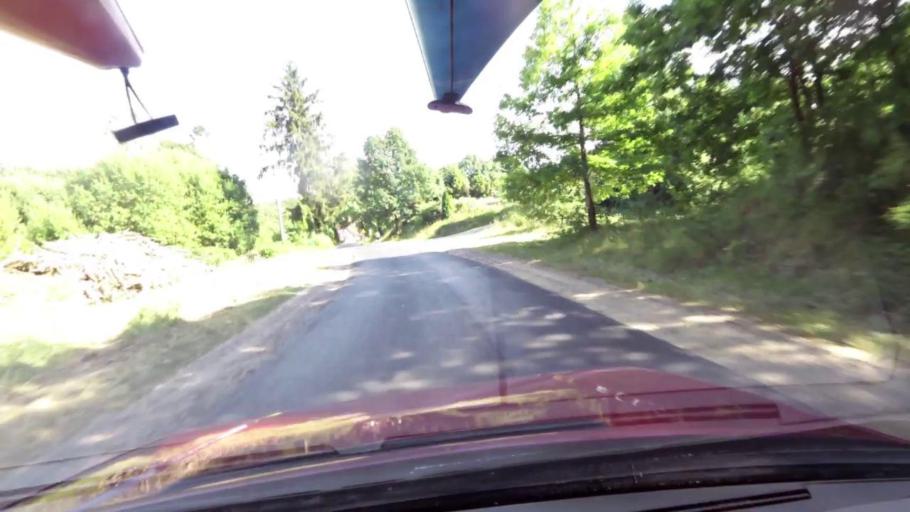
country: PL
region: Pomeranian Voivodeship
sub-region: Powiat bytowski
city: Miastko
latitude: 54.1225
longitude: 16.9436
